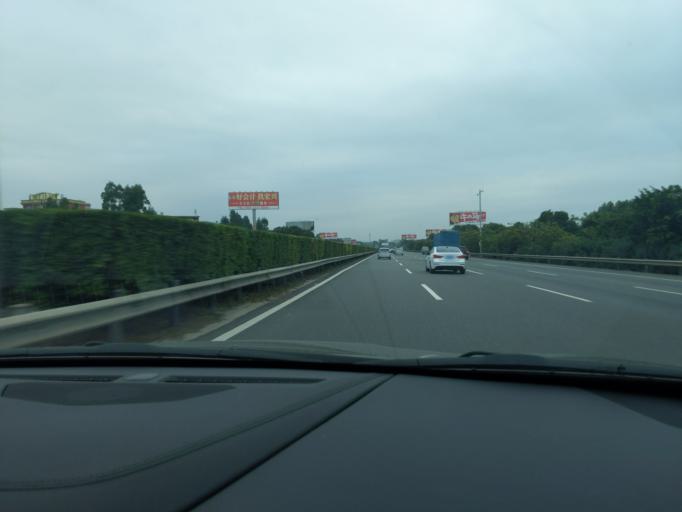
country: CN
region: Fujian
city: Neikeng
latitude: 24.7619
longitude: 118.4483
